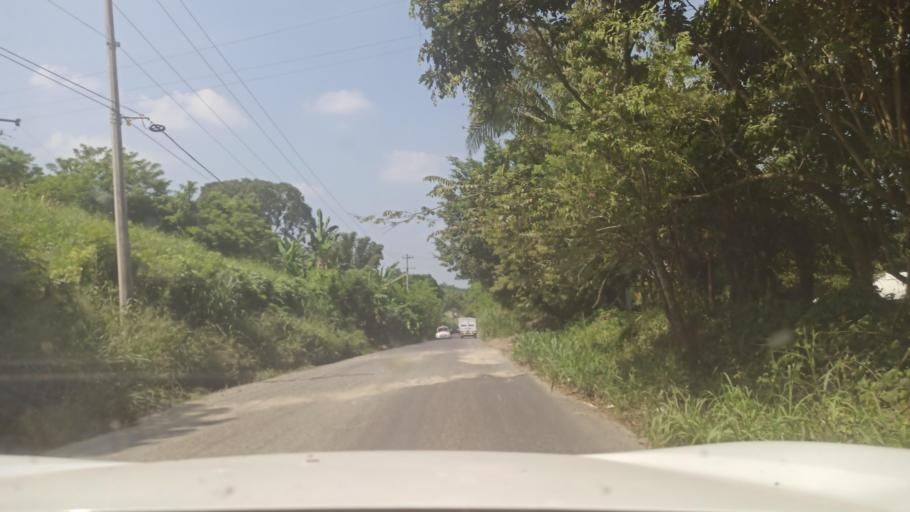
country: MX
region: Veracruz
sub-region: Atzalan
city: Colonias Pedernales
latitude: 20.0468
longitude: -97.0065
